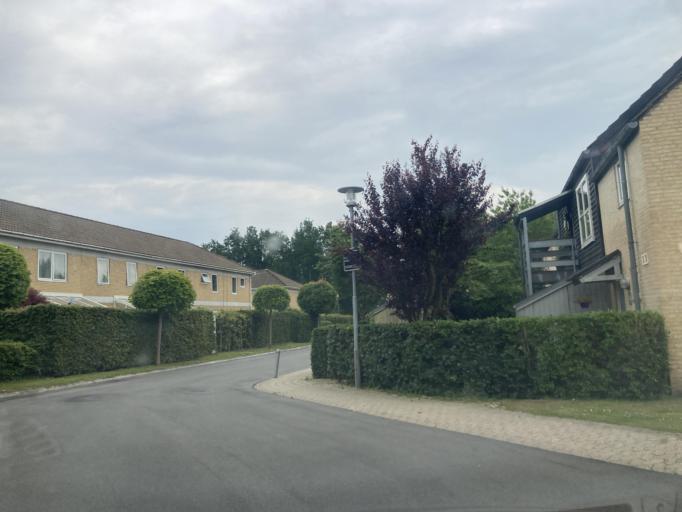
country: DK
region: Capital Region
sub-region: Hoje-Taastrup Kommune
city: Taastrup
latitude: 55.6389
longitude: 12.2788
